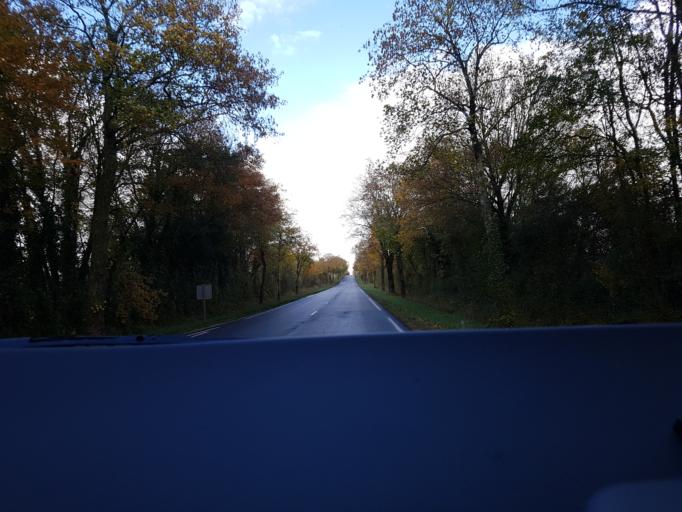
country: FR
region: Poitou-Charentes
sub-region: Departement des Deux-Sevres
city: Brioux-sur-Boutonne
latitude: 46.1022
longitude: -0.2681
